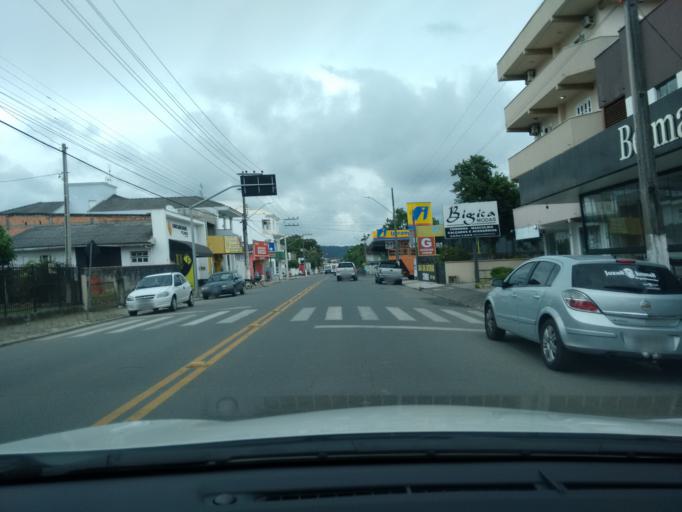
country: BR
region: Santa Catarina
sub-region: Penha
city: Penha
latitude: -26.7586
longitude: -48.6771
